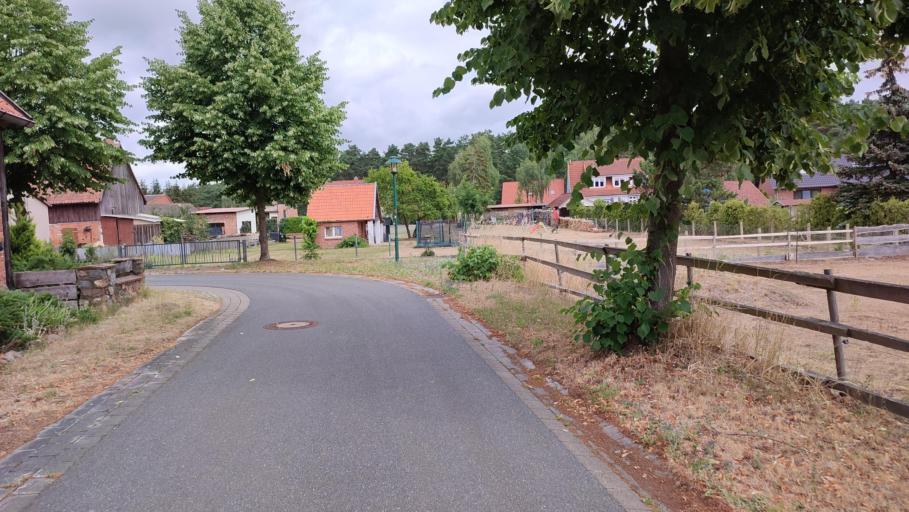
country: DE
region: Lower Saxony
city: Hitzacker
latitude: 53.1842
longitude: 11.1077
